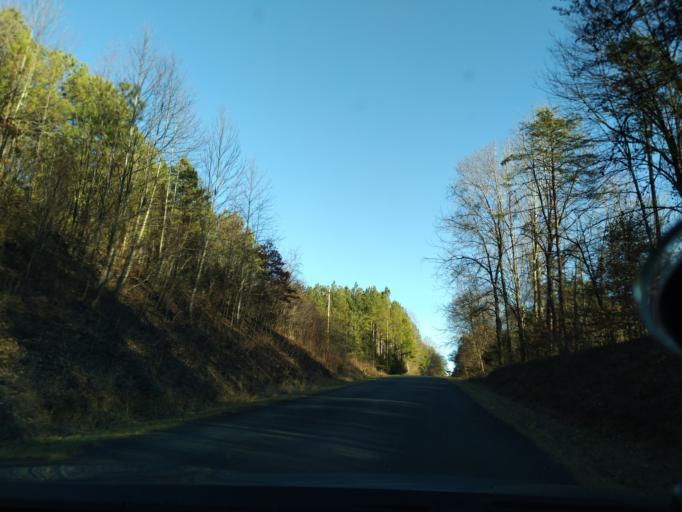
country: US
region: Virginia
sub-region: Buckingham County
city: Buckingham
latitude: 37.3730
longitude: -78.6310
